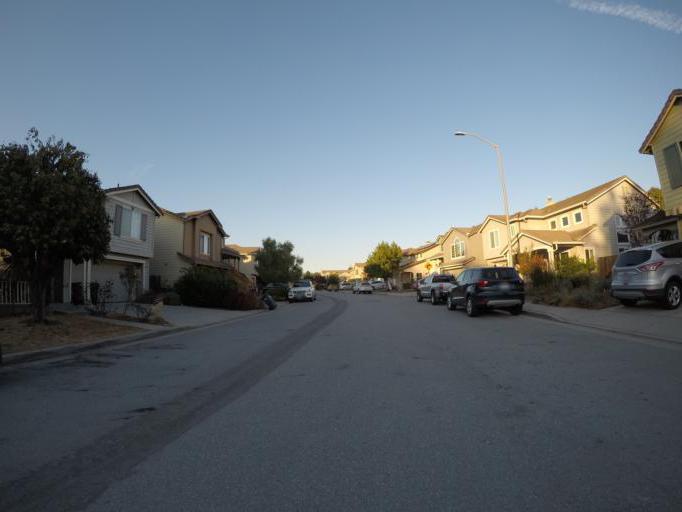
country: US
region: California
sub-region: Santa Cruz County
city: Scotts Valley
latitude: 37.0514
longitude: -122.0351
